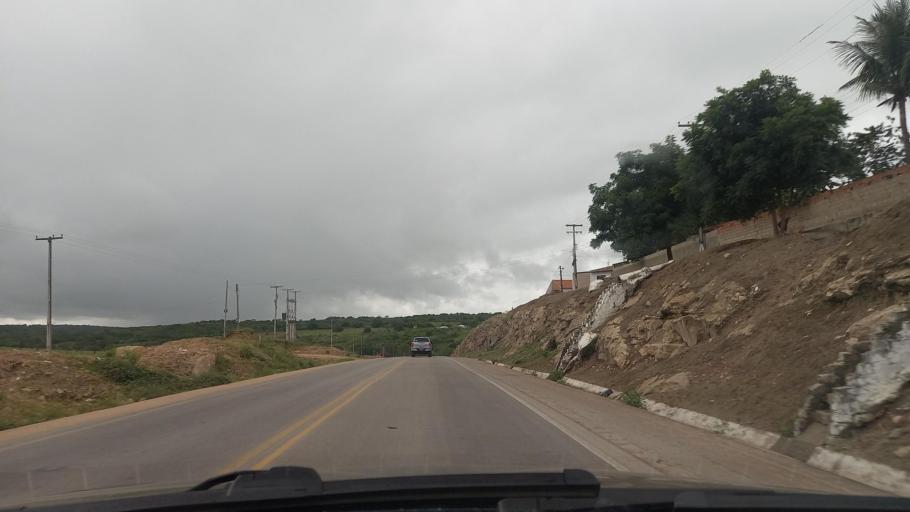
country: BR
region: Alagoas
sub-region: Batalha
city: Batalha
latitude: -9.6314
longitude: -37.2054
